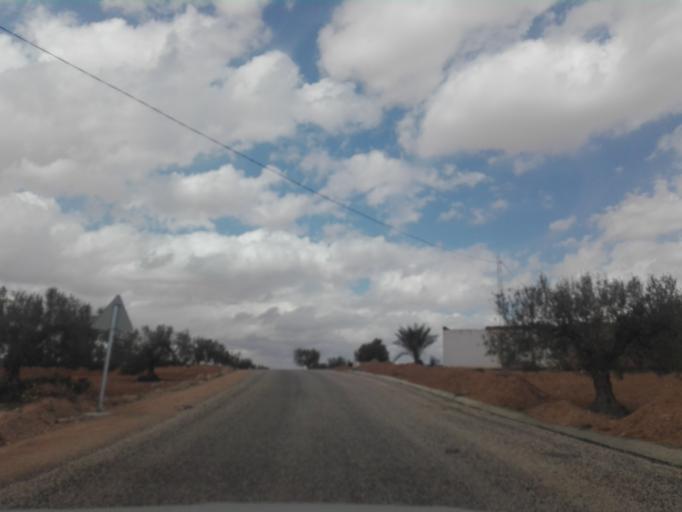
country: TN
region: Safaqis
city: Sfax
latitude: 34.6888
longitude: 10.4488
